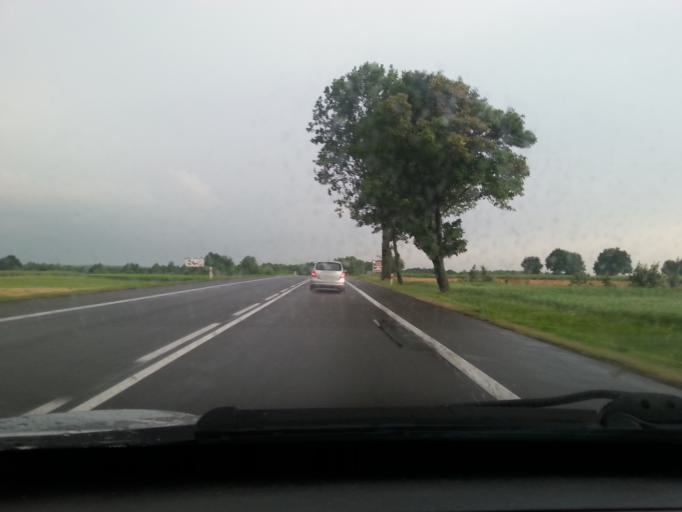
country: PL
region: Lodz Voivodeship
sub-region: Powiat zgierski
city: Strykow
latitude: 51.8504
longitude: 19.5618
